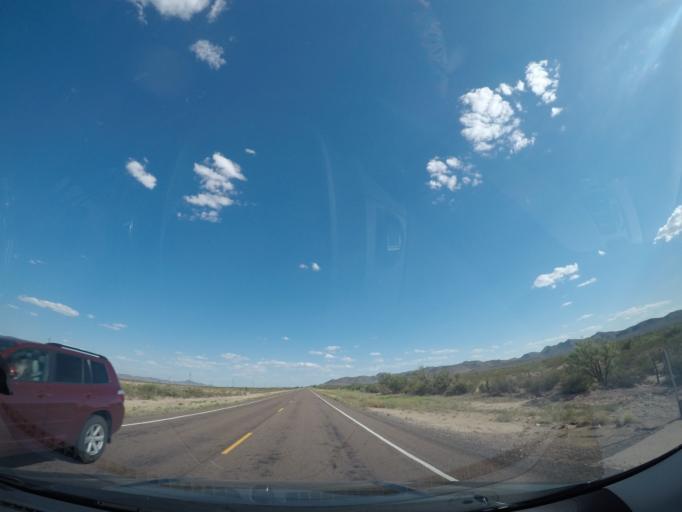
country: US
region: Texas
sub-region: Culberson County
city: Van Horn
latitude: 30.9427
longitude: -104.8116
